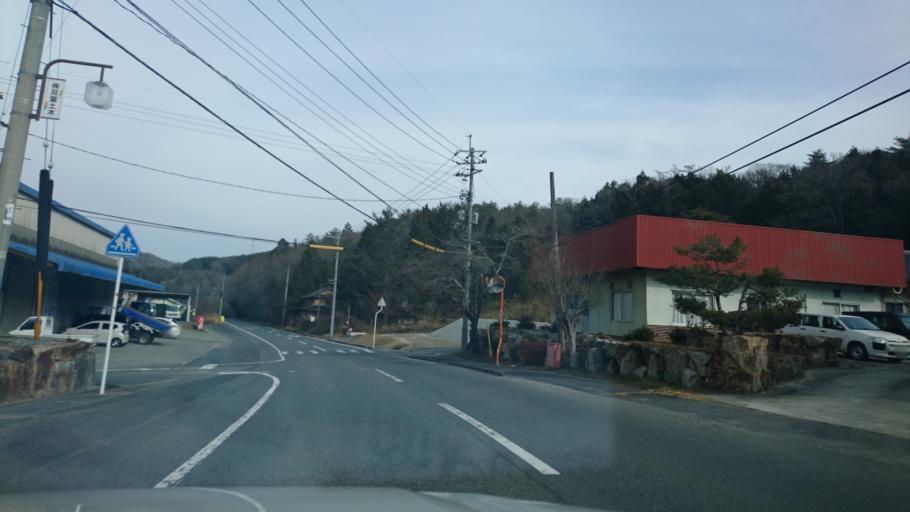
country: JP
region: Okayama
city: Takahashi
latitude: 34.8138
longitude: 133.6745
